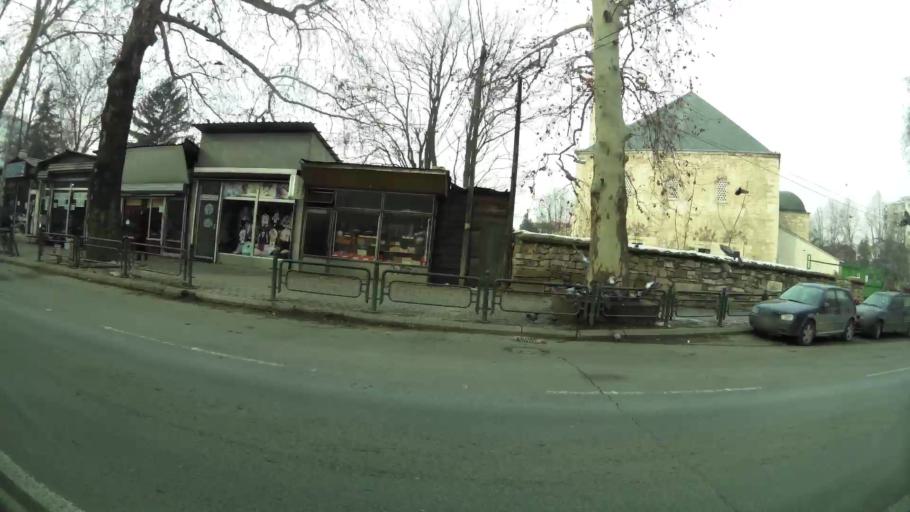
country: MK
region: Cair
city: Cair
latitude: 42.0073
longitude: 21.4426
